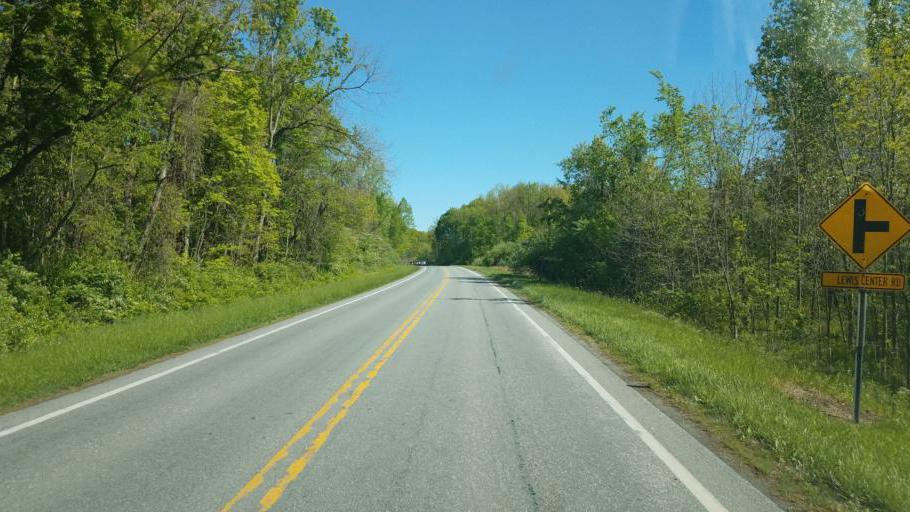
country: US
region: Ohio
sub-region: Delaware County
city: Lewis Center
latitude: 40.1935
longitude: -82.9434
